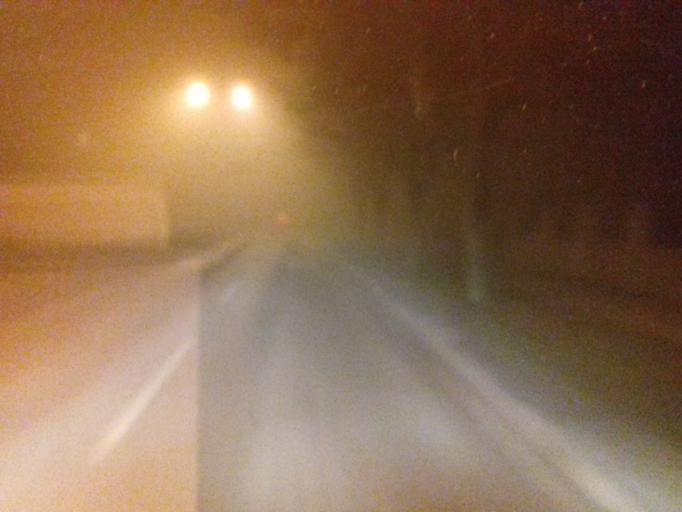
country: BA
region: Federation of Bosnia and Herzegovina
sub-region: Kanton Sarajevo
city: Sarajevo
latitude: 43.8297
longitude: 18.3580
